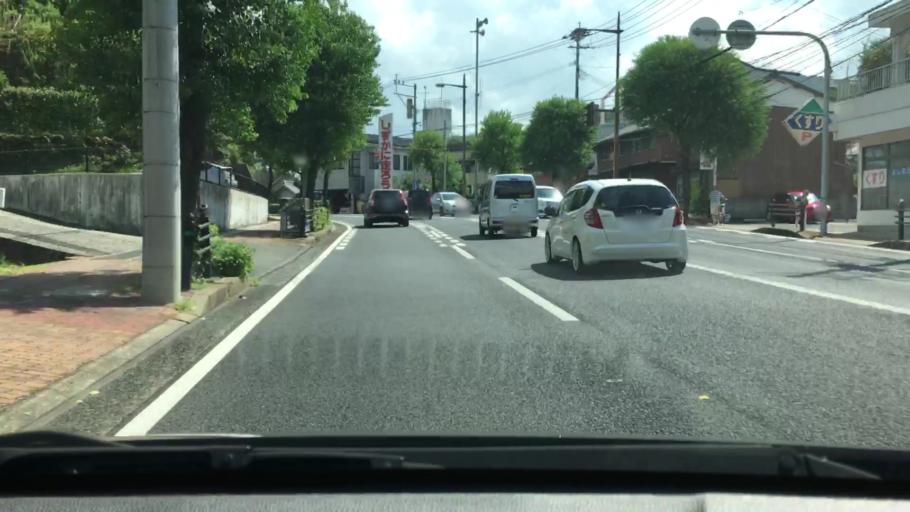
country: JP
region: Nagasaki
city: Sasebo
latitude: 33.2024
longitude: 129.7209
